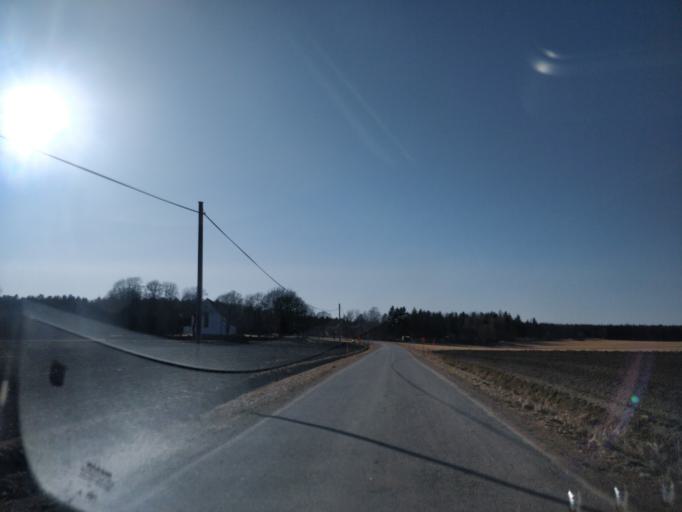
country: SE
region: Uppsala
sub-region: Enkopings Kommun
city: Enkoping
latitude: 59.8141
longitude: 17.1159
